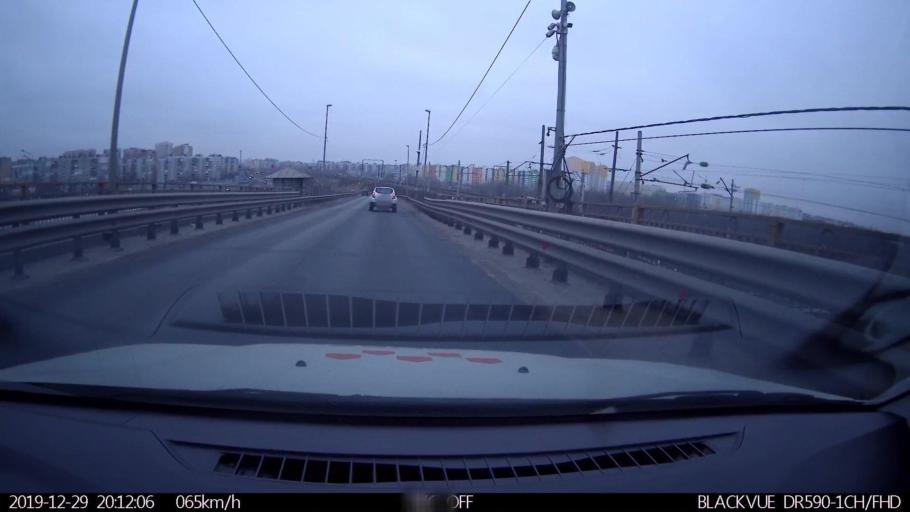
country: RU
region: Nizjnij Novgorod
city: Nizhniy Novgorod
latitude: 56.3495
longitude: 43.9221
